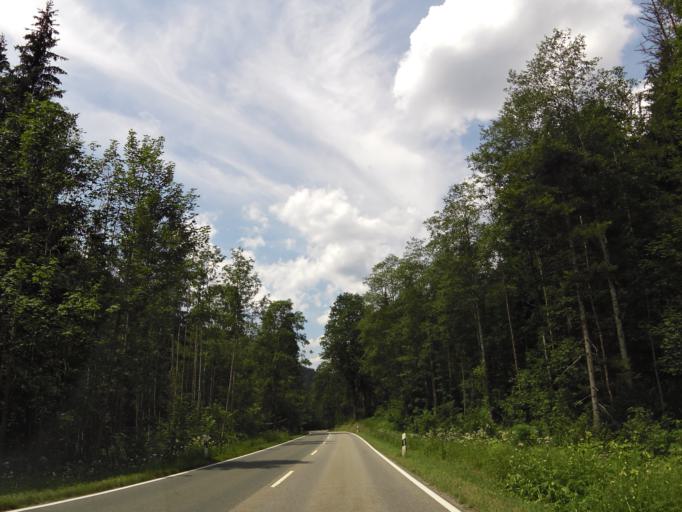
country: DE
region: Bavaria
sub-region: Upper Bavaria
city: Reit im Winkl
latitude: 47.6631
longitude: 12.5110
